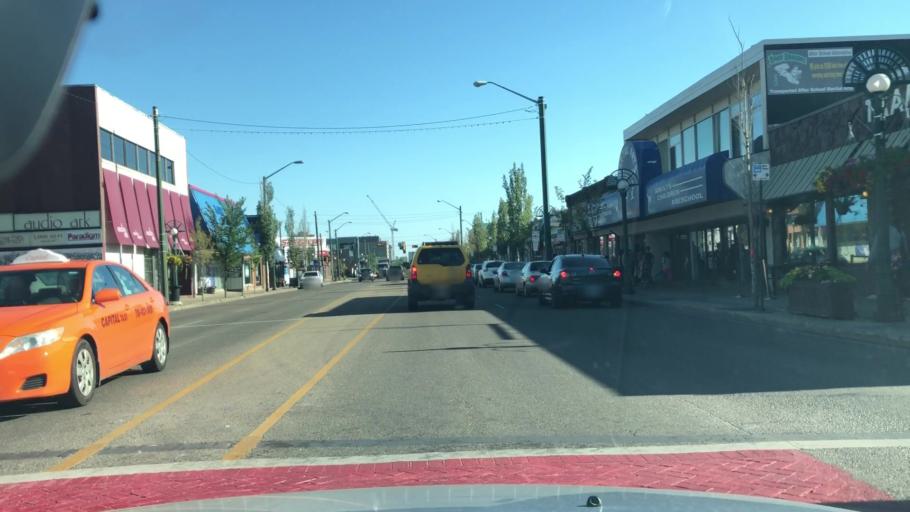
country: CA
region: Alberta
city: Edmonton
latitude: 53.5525
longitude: -113.5359
